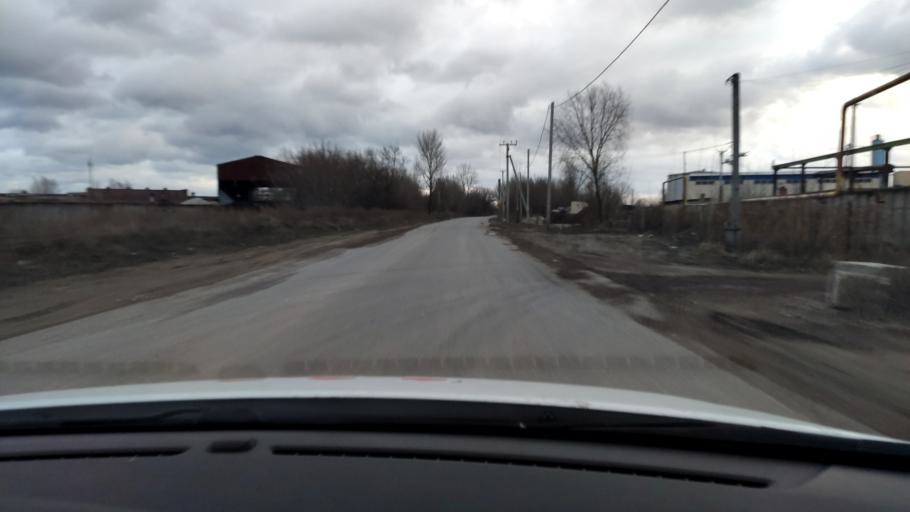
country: RU
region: Tatarstan
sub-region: Gorod Kazan'
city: Kazan
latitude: 55.7270
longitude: 49.0987
